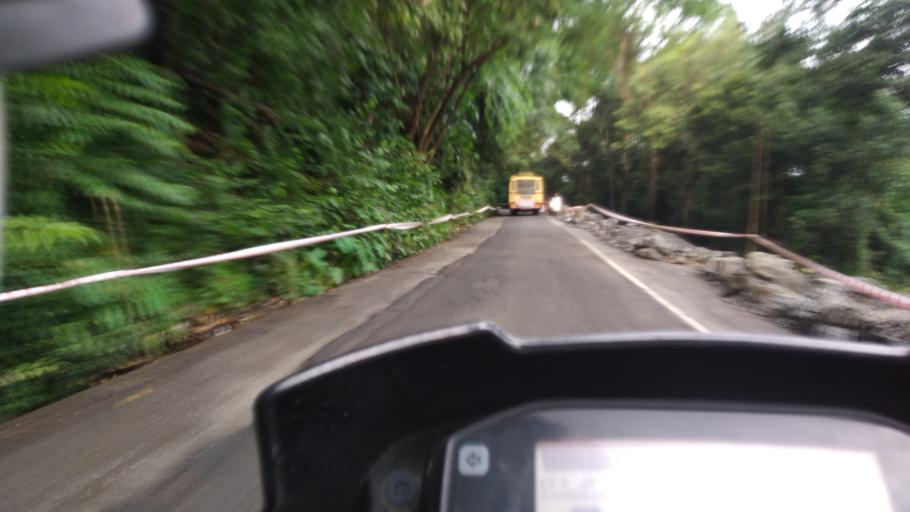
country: IN
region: Kerala
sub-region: Idukki
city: Kuttampuzha
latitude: 10.0661
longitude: 76.7708
